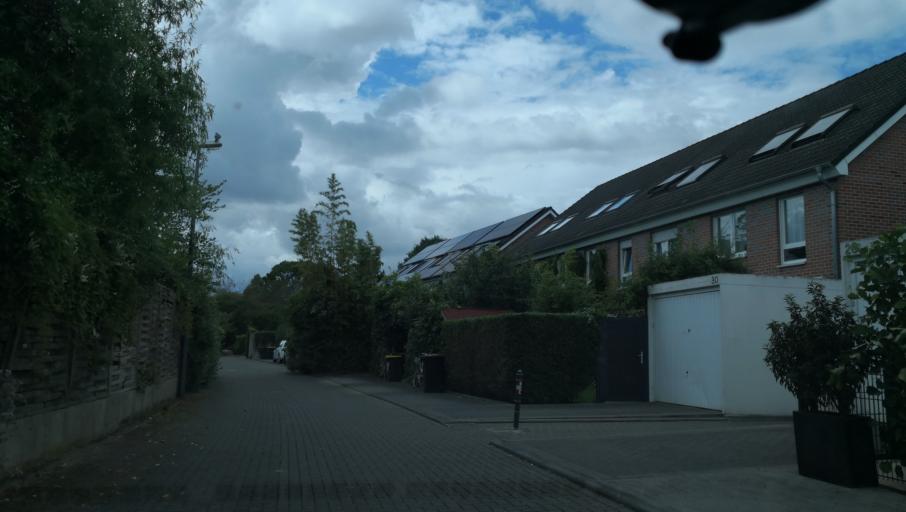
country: DE
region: North Rhine-Westphalia
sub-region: Regierungsbezirk Koln
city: Bilderstoeckchen
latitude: 50.9713
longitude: 6.9101
